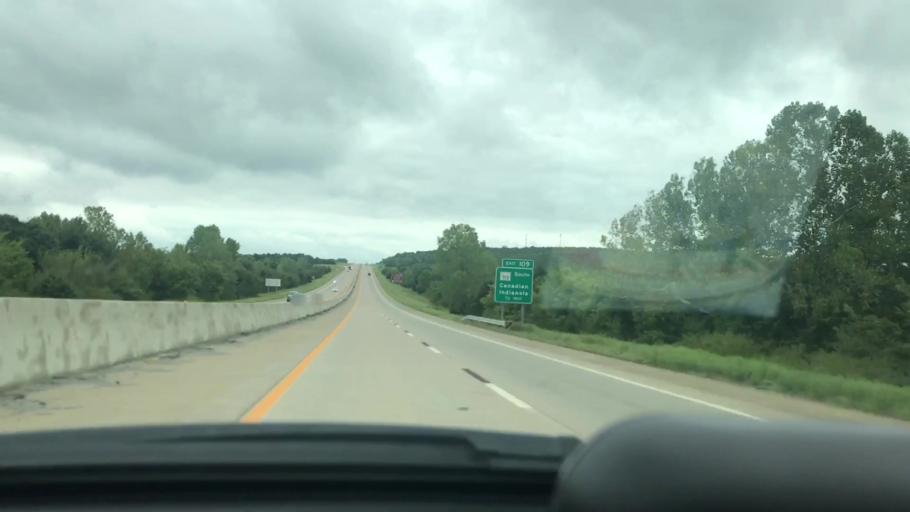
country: US
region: Oklahoma
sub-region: McIntosh County
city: Eufaula
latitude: 35.1607
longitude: -95.6556
